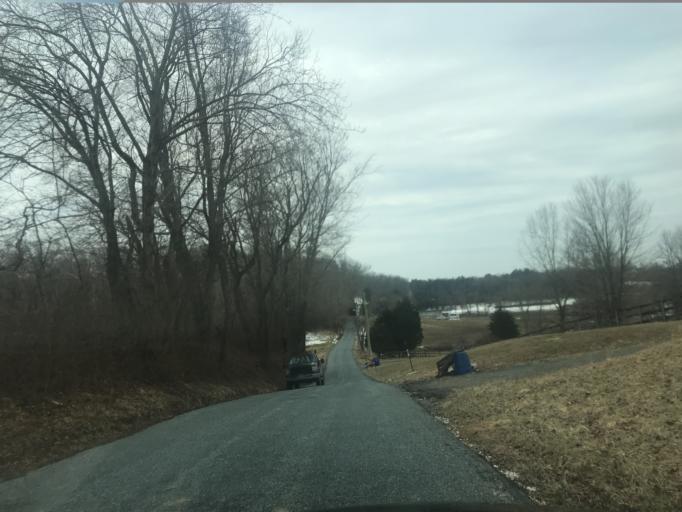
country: US
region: Pennsylvania
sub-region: York County
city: Susquehanna Trails
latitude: 39.6940
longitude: -76.4182
